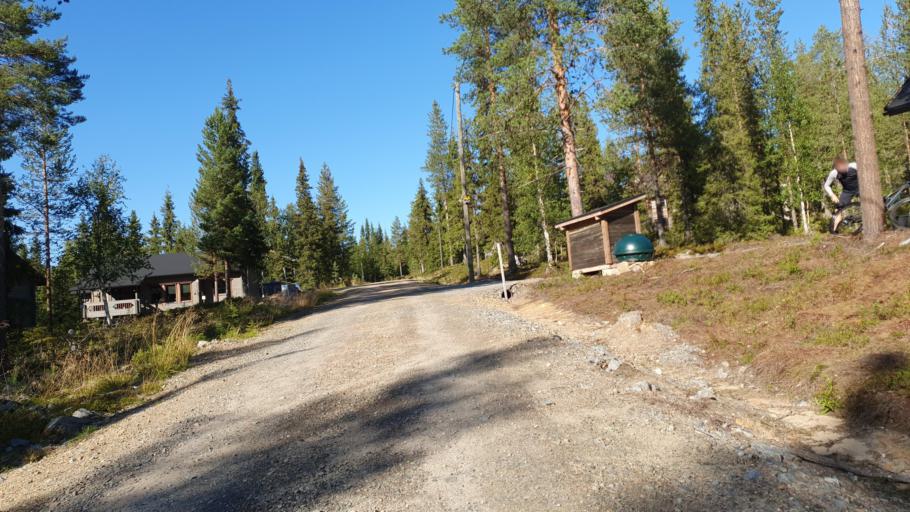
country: FI
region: Lapland
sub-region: Tunturi-Lappi
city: Kolari
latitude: 67.6058
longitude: 24.2060
